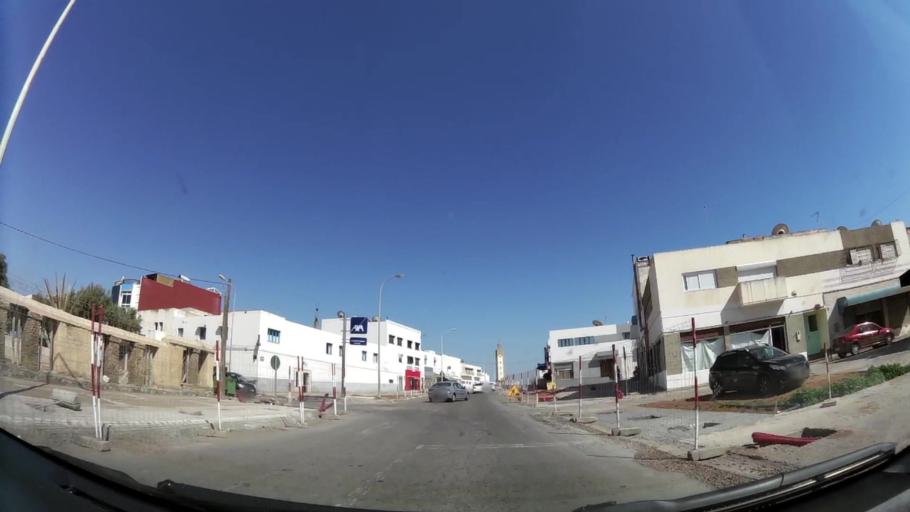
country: MA
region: Souss-Massa-Draa
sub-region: Agadir-Ida-ou-Tnan
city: Agadir
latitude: 30.4236
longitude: -9.5963
